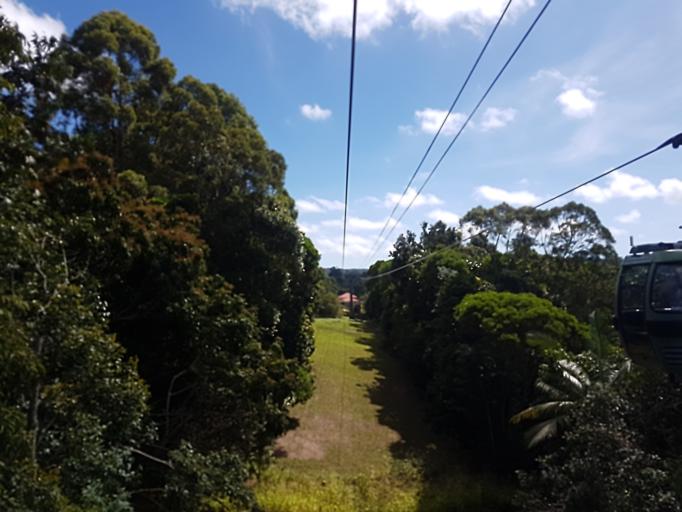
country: AU
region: Queensland
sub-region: Tablelands
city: Kuranda
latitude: -16.8212
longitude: 145.6401
